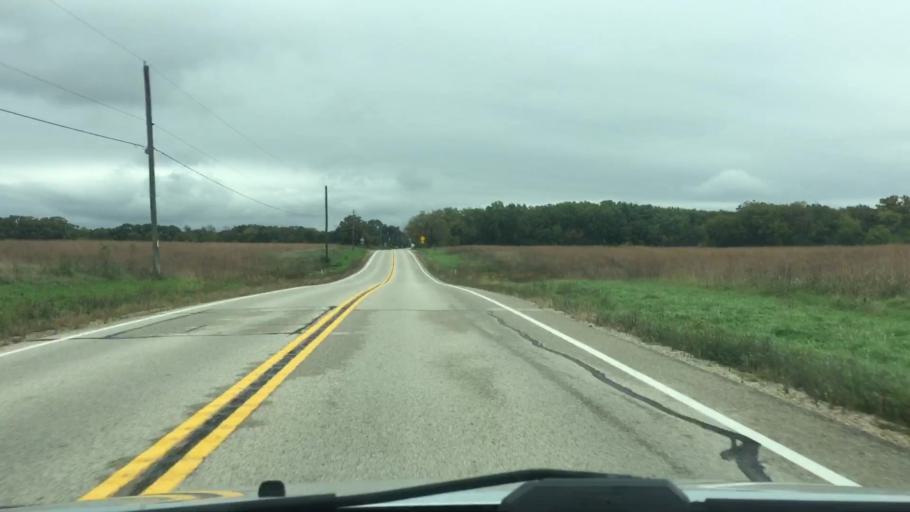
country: US
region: Wisconsin
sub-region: Waukesha County
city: Eagle
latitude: 42.8915
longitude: -88.4737
